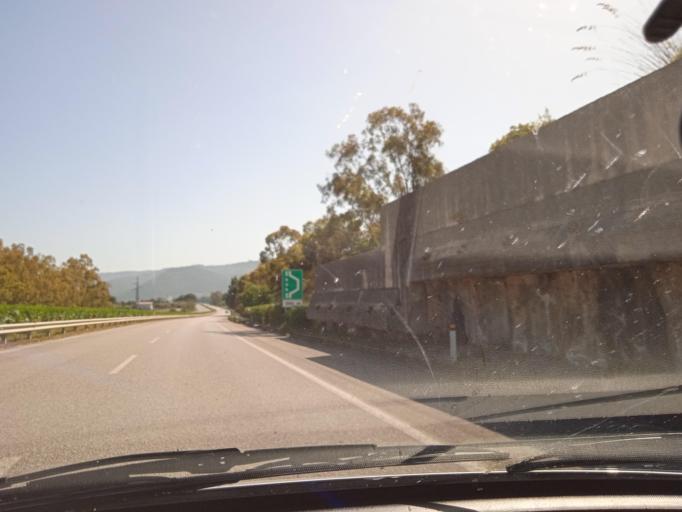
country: IT
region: Sicily
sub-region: Messina
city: Rocca di Capri Leone
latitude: 38.0929
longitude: 14.6984
